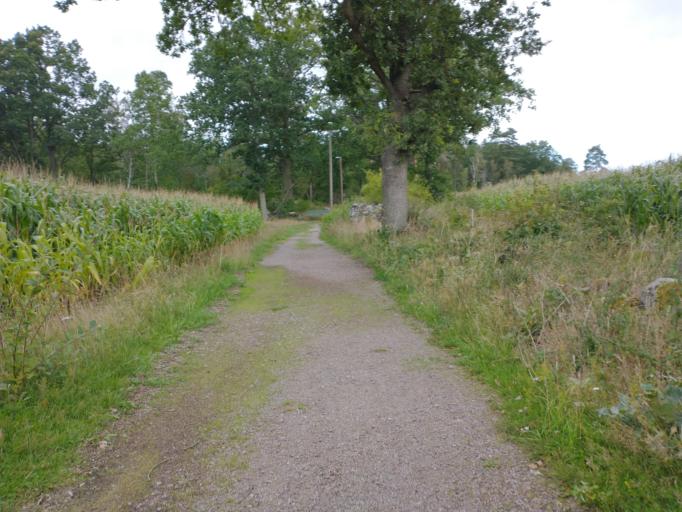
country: SE
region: Kalmar
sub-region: Kalmar Kommun
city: Lindsdal
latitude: 56.7761
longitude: 16.3001
